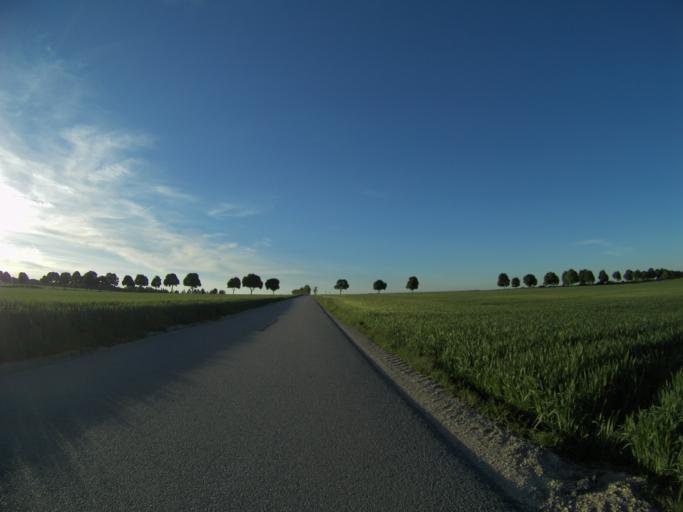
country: DE
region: Bavaria
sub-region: Upper Bavaria
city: Langenbach
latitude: 48.4411
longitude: 11.8826
